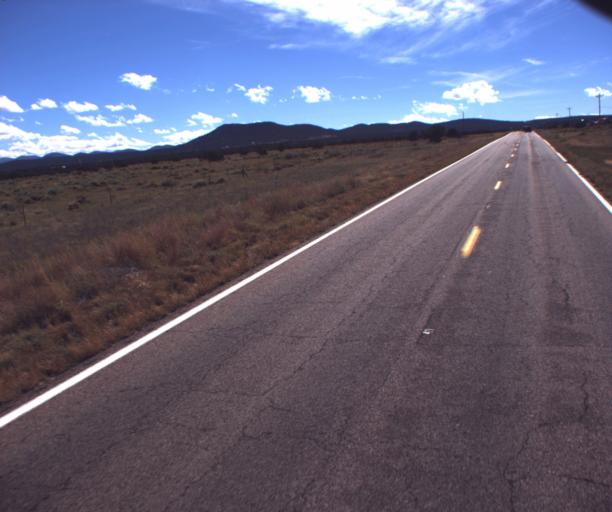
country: US
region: Arizona
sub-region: Navajo County
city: White Mountain Lake
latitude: 34.3460
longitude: -109.7262
